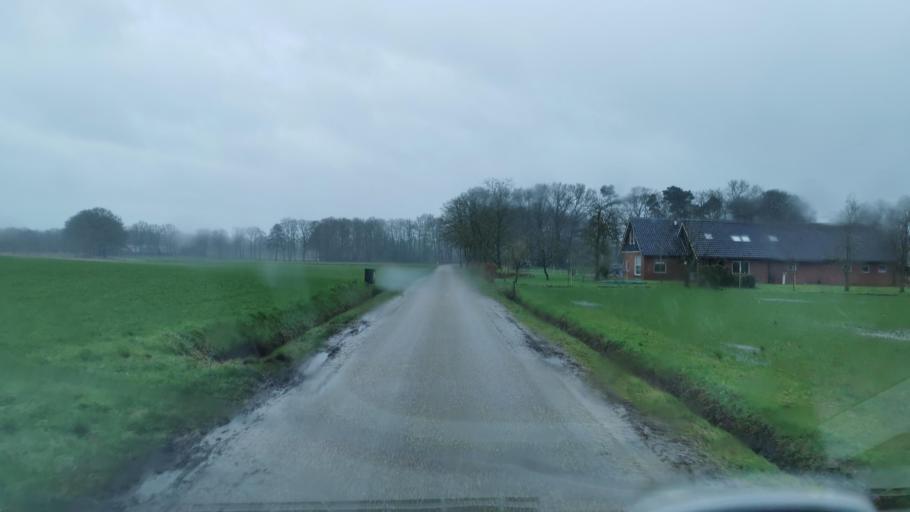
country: NL
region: Overijssel
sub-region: Gemeente Tubbergen
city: Tubbergen
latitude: 52.3722
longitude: 6.7966
